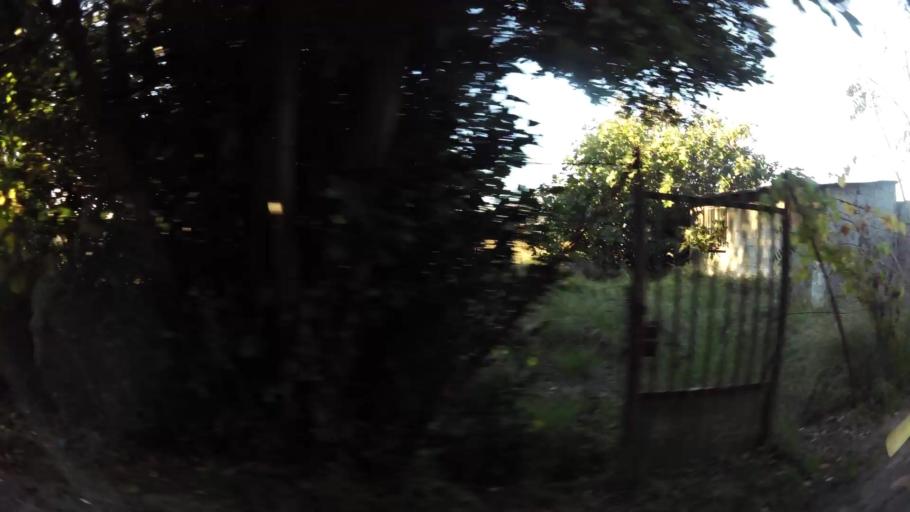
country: GR
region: Attica
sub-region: Nomarchia Anatolikis Attikis
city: Pallini
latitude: 38.0041
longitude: 23.8625
